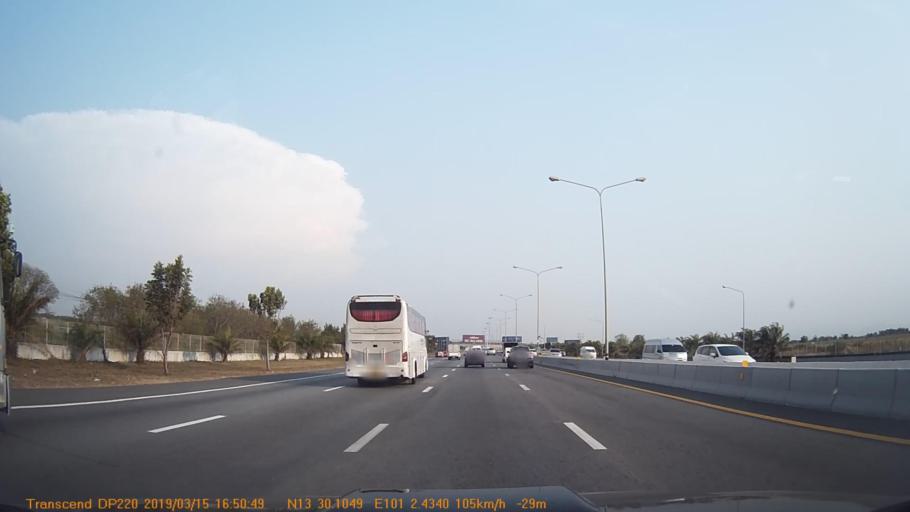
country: TH
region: Chon Buri
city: Phan Thong
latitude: 13.5010
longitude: 101.0414
